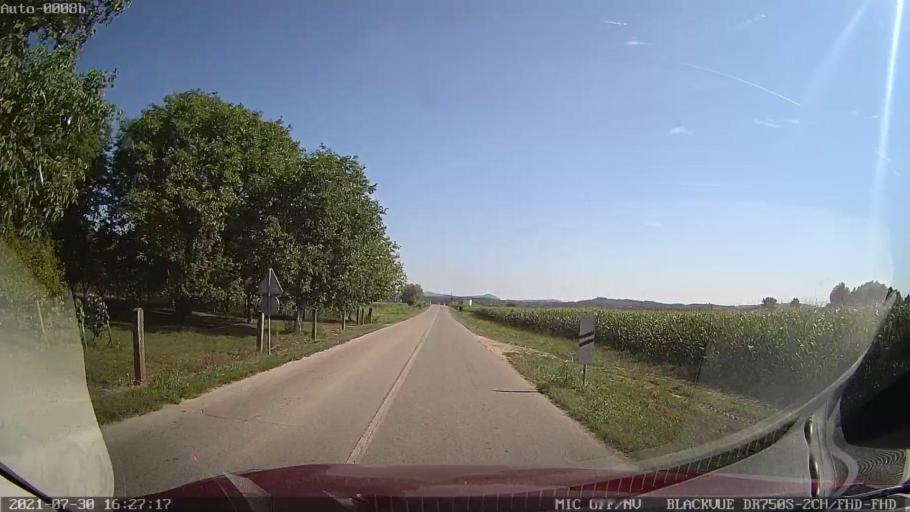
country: HR
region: Varazdinska
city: Jalzabet
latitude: 46.2766
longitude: 16.4335
